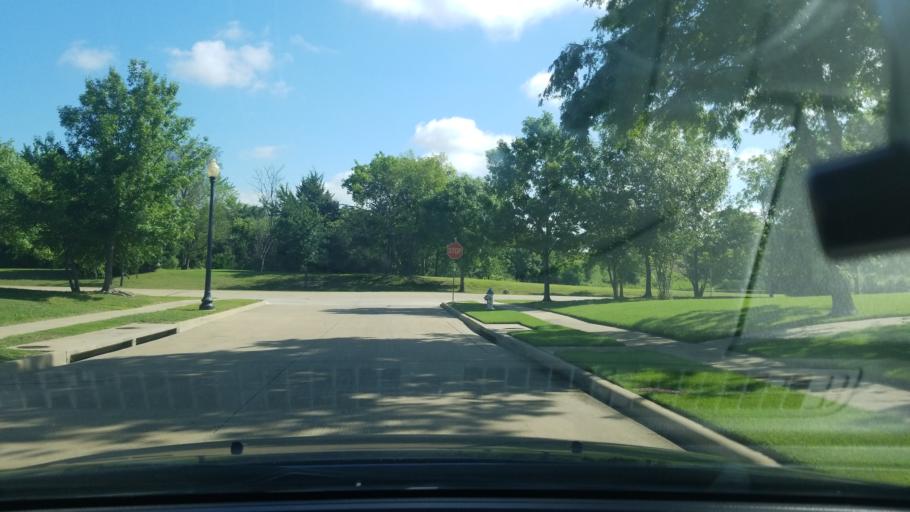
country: US
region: Texas
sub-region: Dallas County
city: Sunnyvale
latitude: 32.8099
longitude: -96.5851
